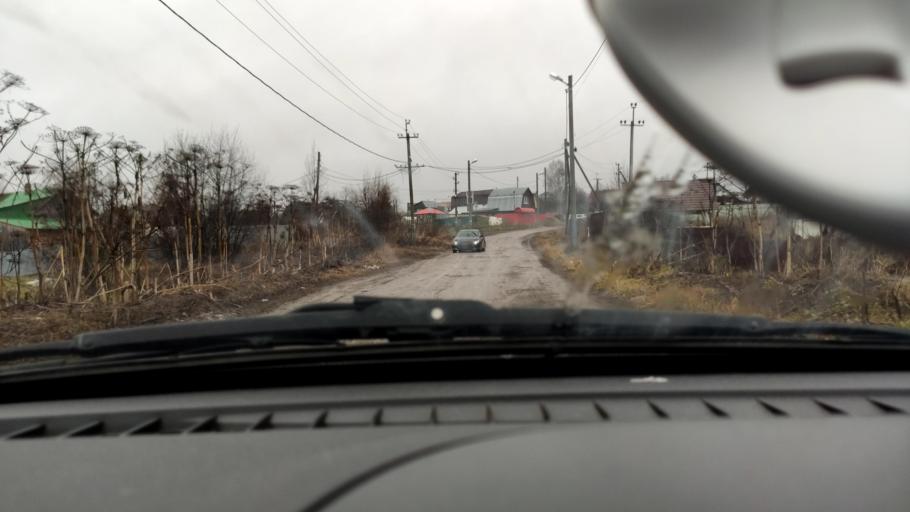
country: RU
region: Perm
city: Perm
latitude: 58.0355
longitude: 56.4096
